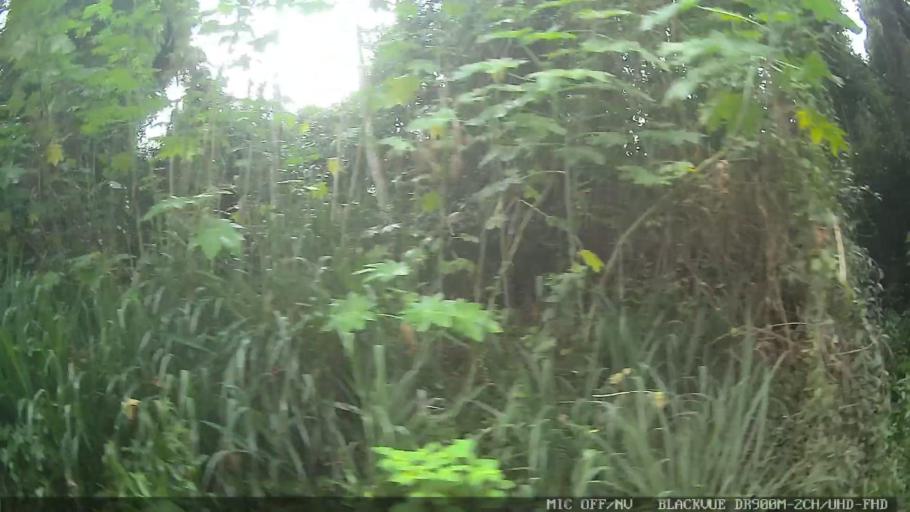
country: BR
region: Sao Paulo
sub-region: Atibaia
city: Atibaia
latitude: -23.1640
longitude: -46.6247
